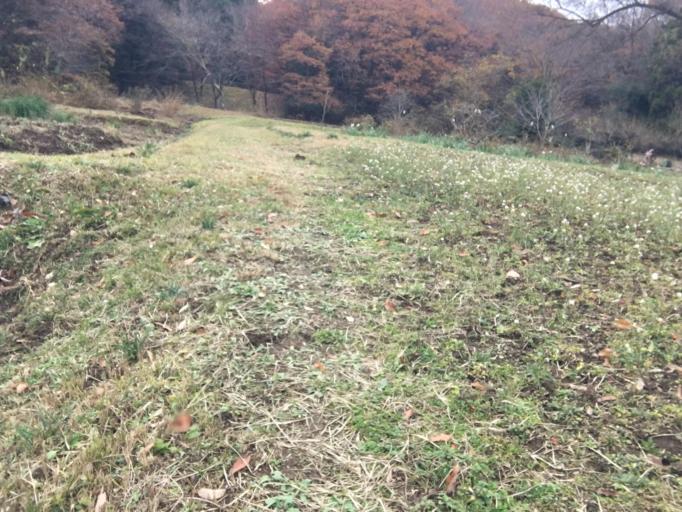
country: JP
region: Saitama
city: Yorii
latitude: 36.1324
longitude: 139.1987
